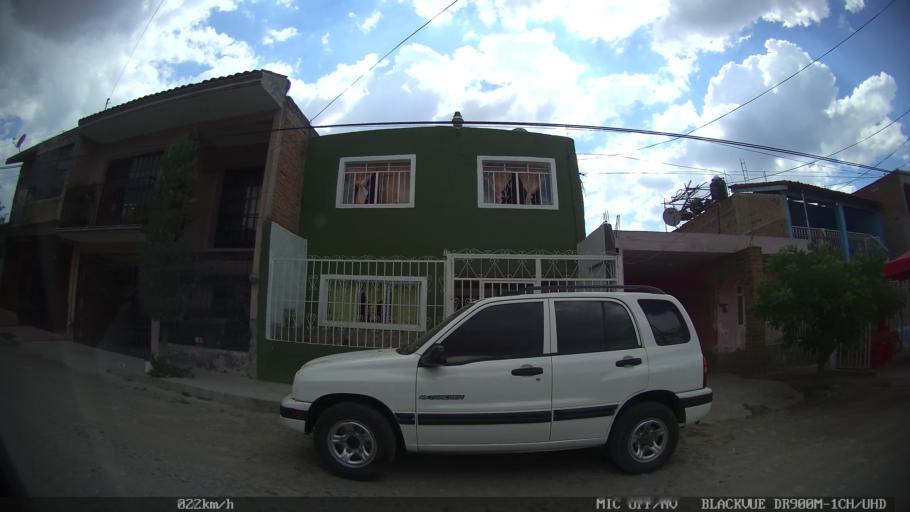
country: MX
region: Jalisco
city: Tlaquepaque
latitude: 20.6843
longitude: -103.2621
